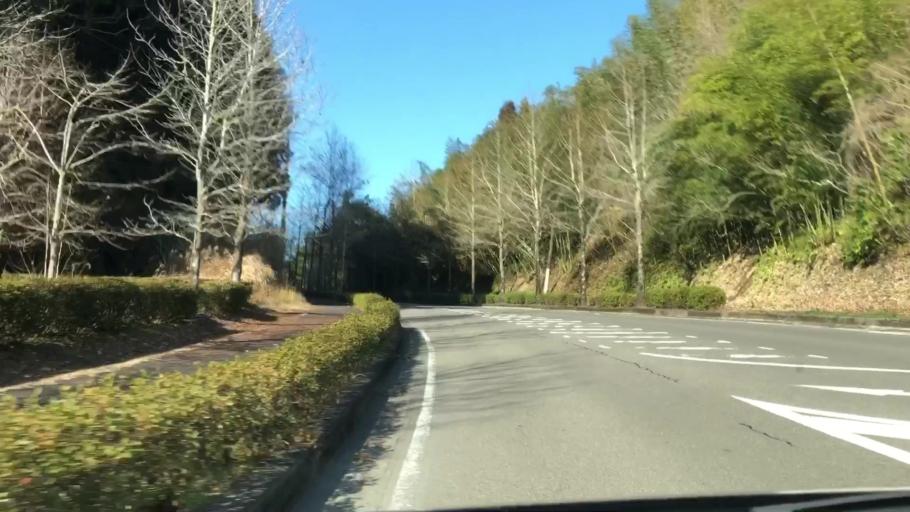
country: JP
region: Kagoshima
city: Satsumasendai
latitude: 31.8281
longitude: 130.4353
